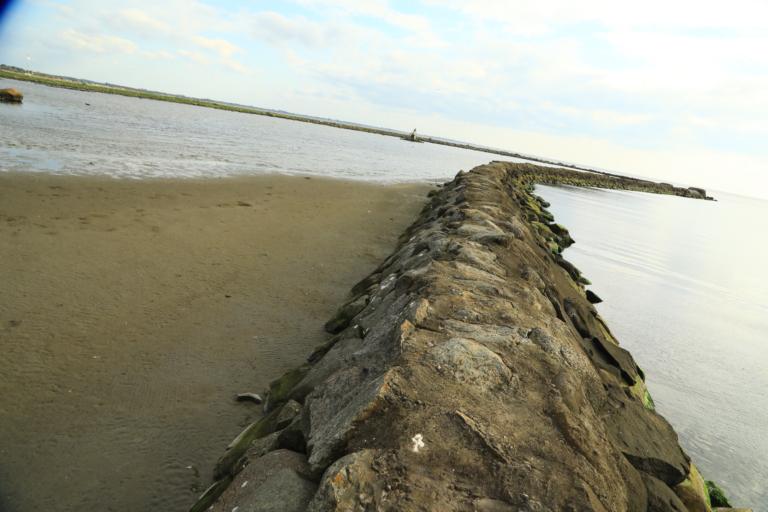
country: SE
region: Halland
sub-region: Varbergs Kommun
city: Traslovslage
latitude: 57.0275
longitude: 12.3084
